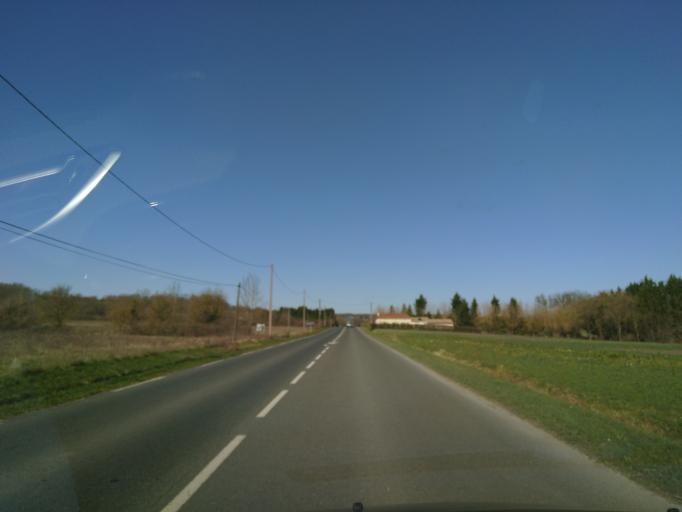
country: FR
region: Aquitaine
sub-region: Departement du Lot-et-Garonne
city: Castillonnes
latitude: 44.7094
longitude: 0.5606
